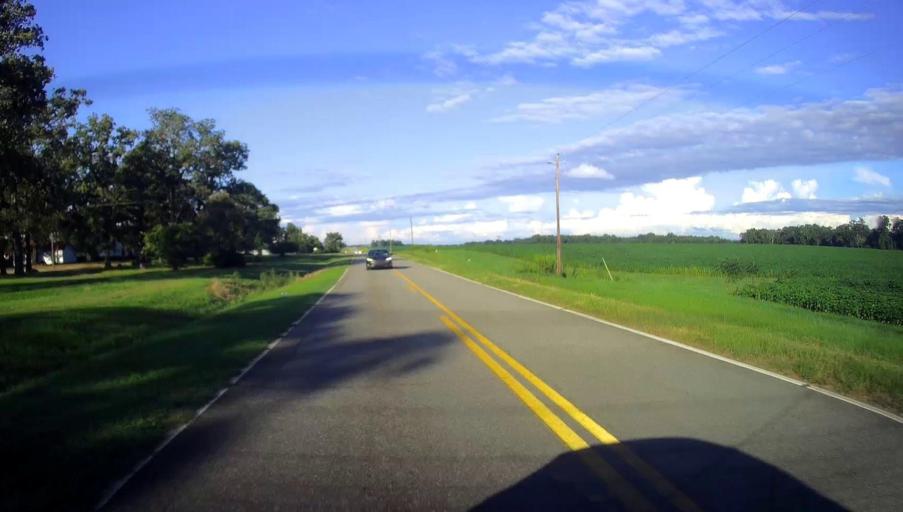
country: US
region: Georgia
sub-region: Bleckley County
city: Cochran
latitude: 32.4008
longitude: -83.4273
